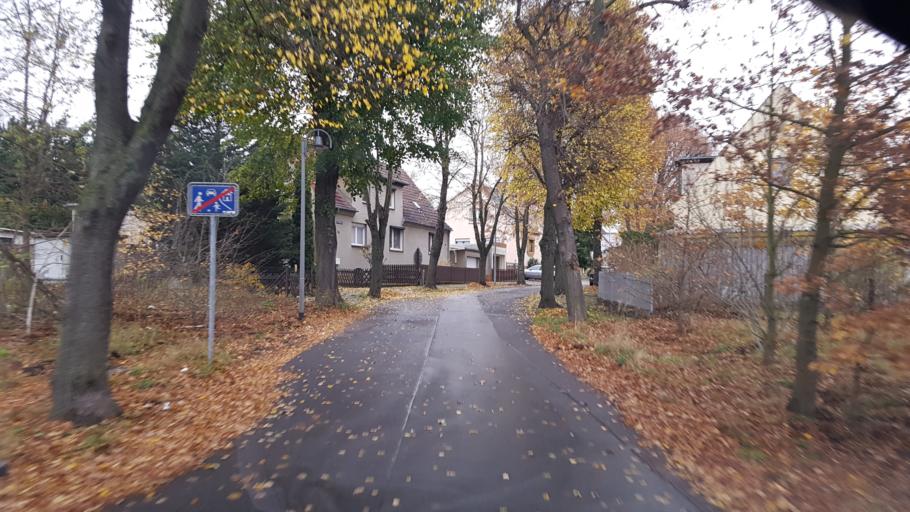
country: DE
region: Brandenburg
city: Lauchhammer
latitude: 51.4928
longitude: 13.7439
